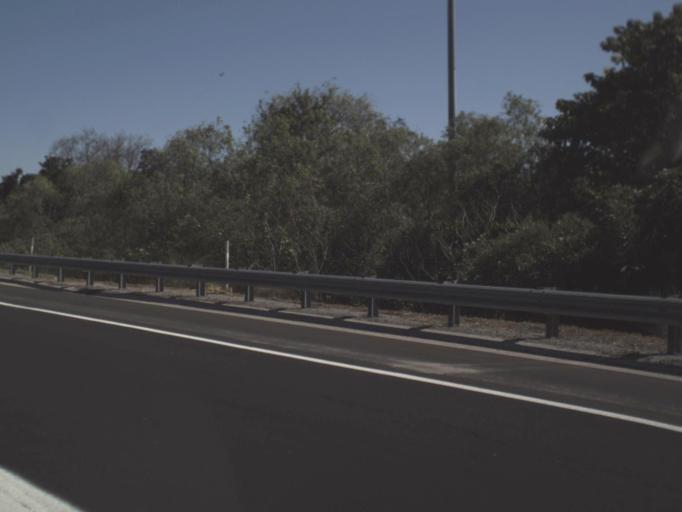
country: US
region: Florida
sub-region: Seminole County
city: Lake Mary
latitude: 28.7988
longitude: -81.3227
